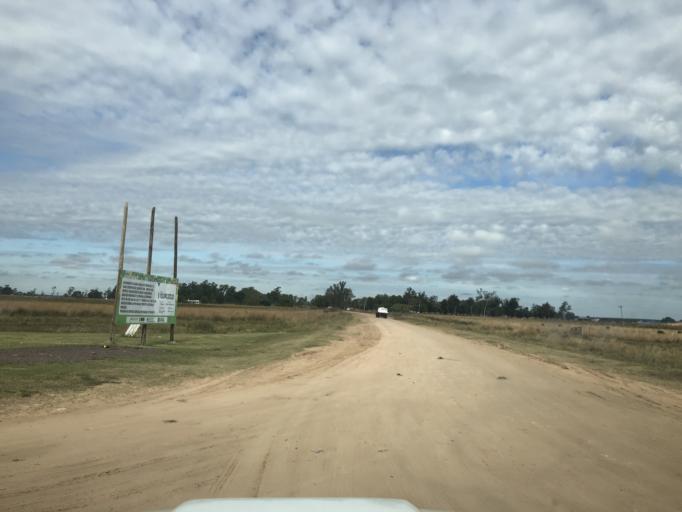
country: AR
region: Corrientes
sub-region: Departamento de Concepcion
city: Concepcion
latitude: -28.3843
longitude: -57.9056
